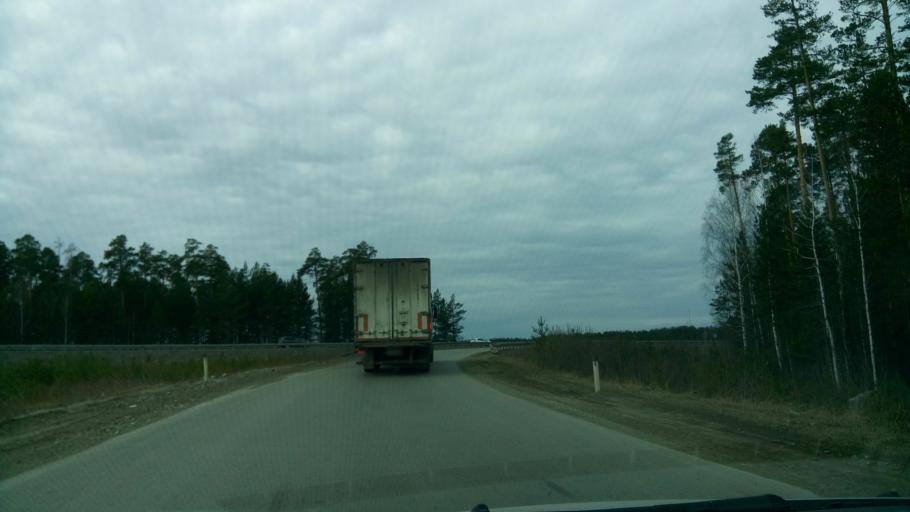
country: RU
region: Sverdlovsk
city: Verkhnyaya Pyshma
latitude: 56.9486
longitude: 60.6326
